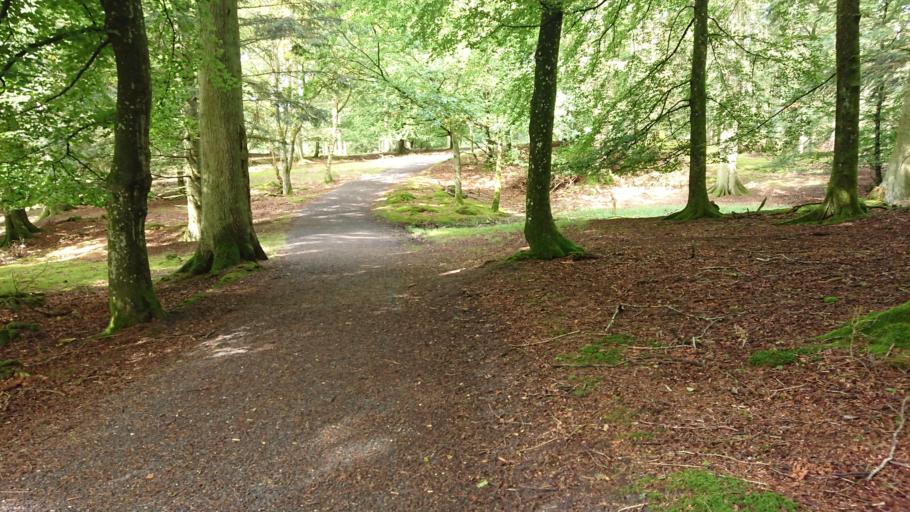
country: DK
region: North Denmark
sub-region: Hjorring Kommune
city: Sindal
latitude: 57.4752
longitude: 10.1717
